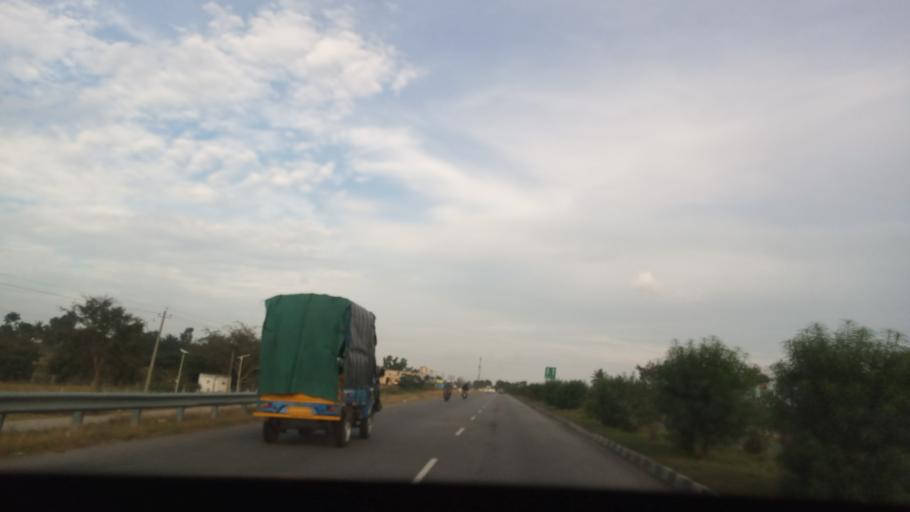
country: IN
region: Karnataka
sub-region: Bangalore Rural
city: Nelamangala
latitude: 13.0608
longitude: 77.3385
